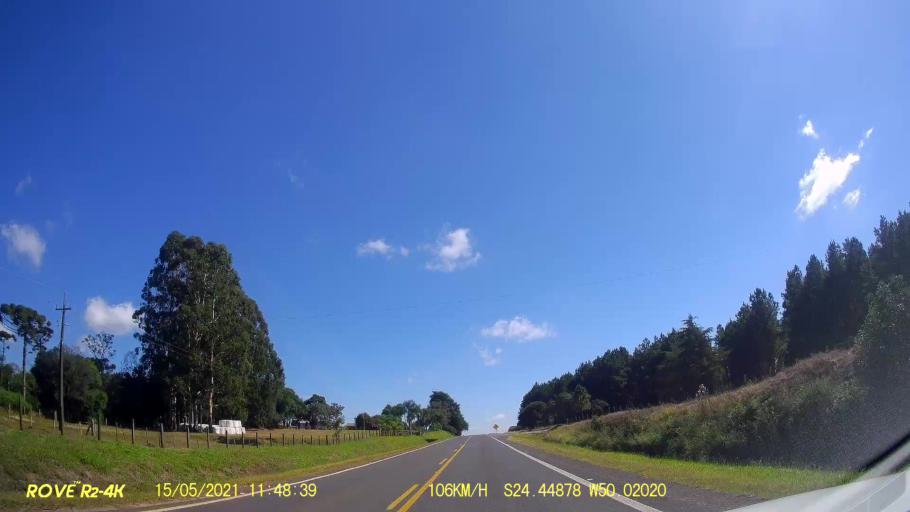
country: BR
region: Parana
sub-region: Pirai Do Sul
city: Pirai do Sul
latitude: -24.4488
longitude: -50.0202
